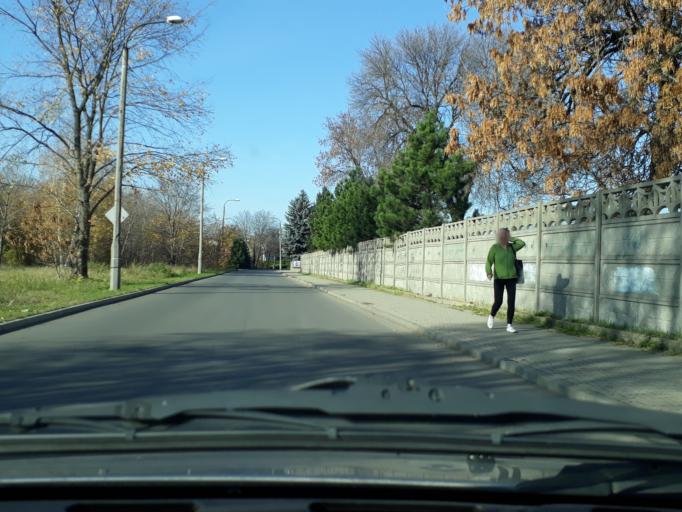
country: PL
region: Silesian Voivodeship
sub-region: Powiat tarnogorski
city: Tarnowskie Gory
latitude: 50.4240
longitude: 18.8759
